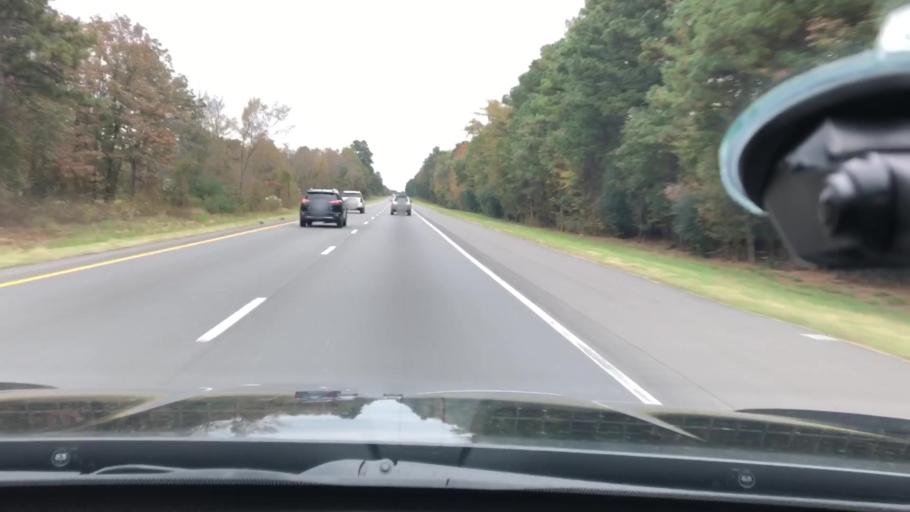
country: US
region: Arkansas
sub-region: Hempstead County
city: Hope
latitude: 33.7057
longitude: -93.5778
